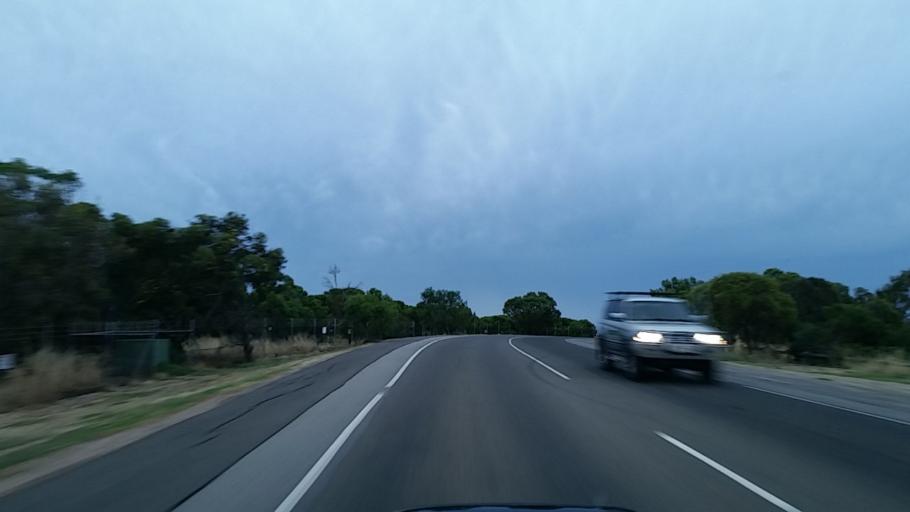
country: AU
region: South Australia
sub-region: Adelaide
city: Port Noarlunga
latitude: -35.1239
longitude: 138.4733
